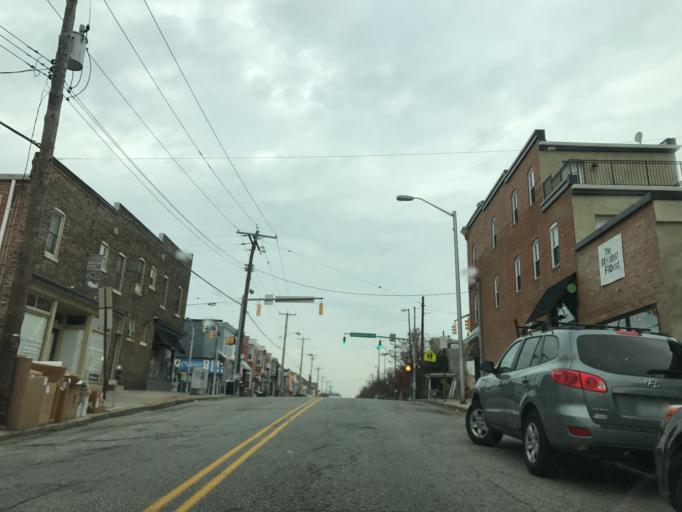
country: US
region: Maryland
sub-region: City of Baltimore
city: Baltimore
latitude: 39.3313
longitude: -76.6288
